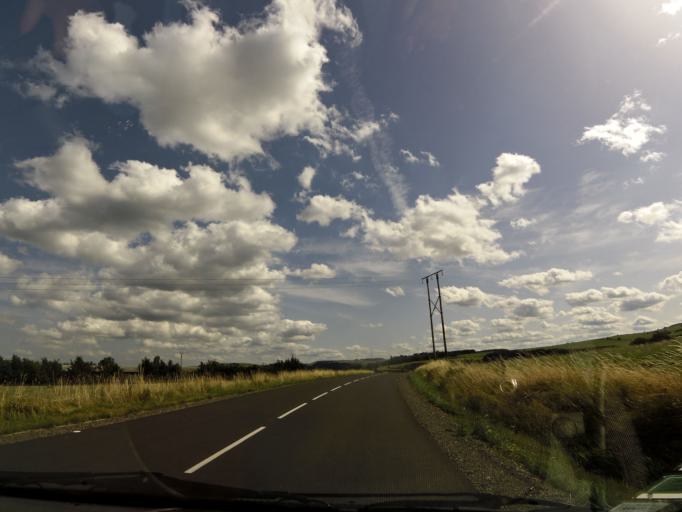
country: FR
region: Auvergne
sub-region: Departement du Puy-de-Dome
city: Aydat
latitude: 45.5483
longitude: 2.9451
